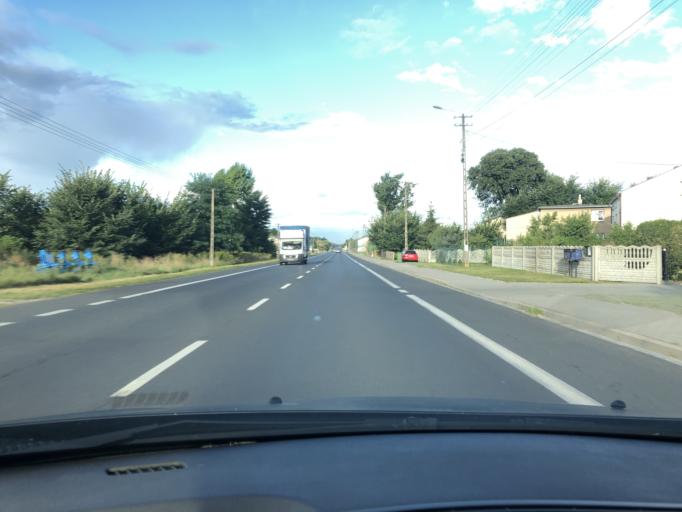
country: PL
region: Lodz Voivodeship
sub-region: Powiat wieruszowski
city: Wieruszow
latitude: 51.2984
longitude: 18.2056
